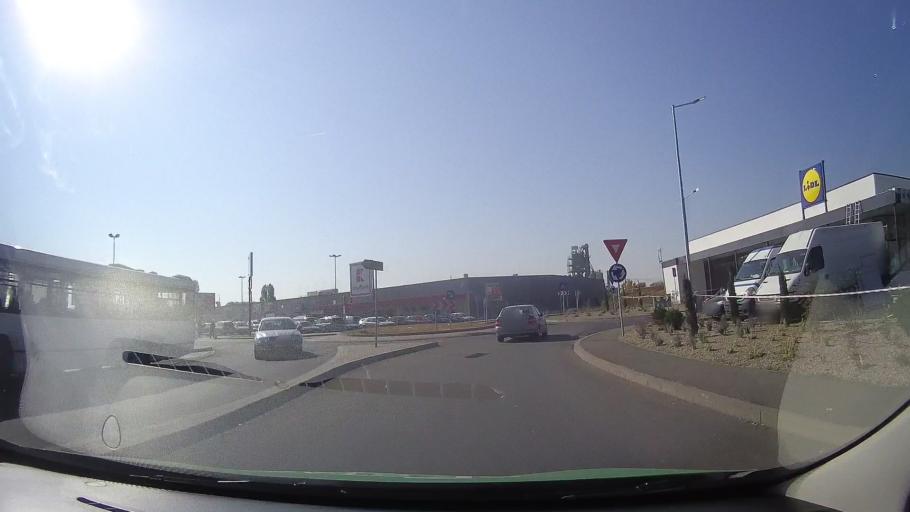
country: RO
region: Bihor
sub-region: Comuna Biharea
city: Oradea
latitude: 47.0760
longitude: 21.9026
